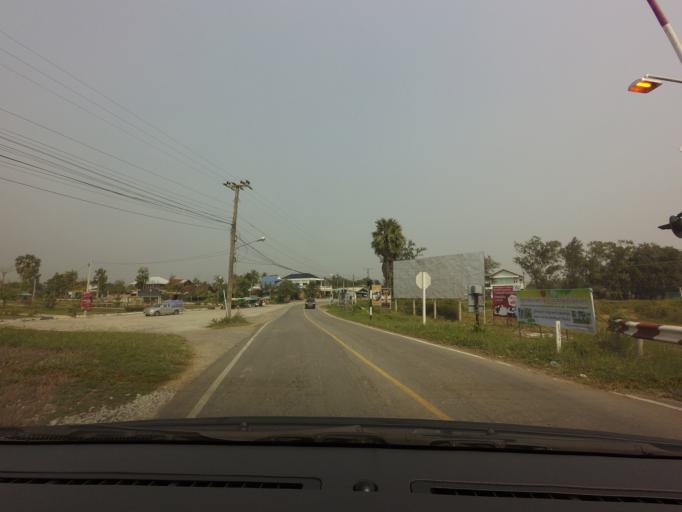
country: TH
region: Prachuap Khiri Khan
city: Kui Buri
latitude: 12.0678
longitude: 99.8723
